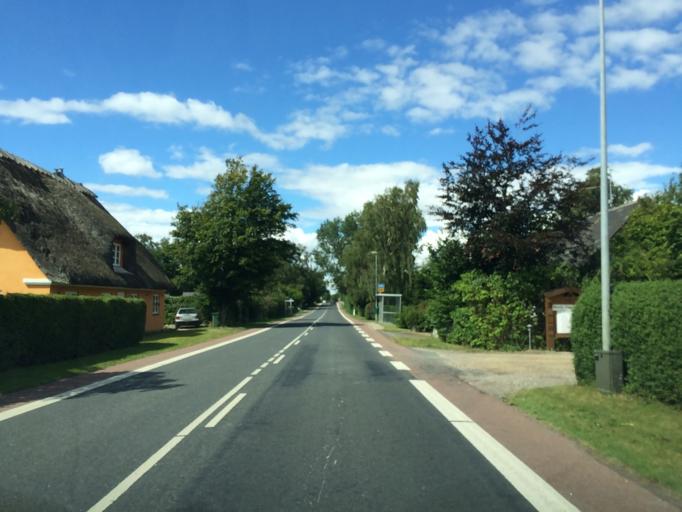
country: DK
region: South Denmark
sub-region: Assens Kommune
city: Harby
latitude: 55.1420
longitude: 10.1613
